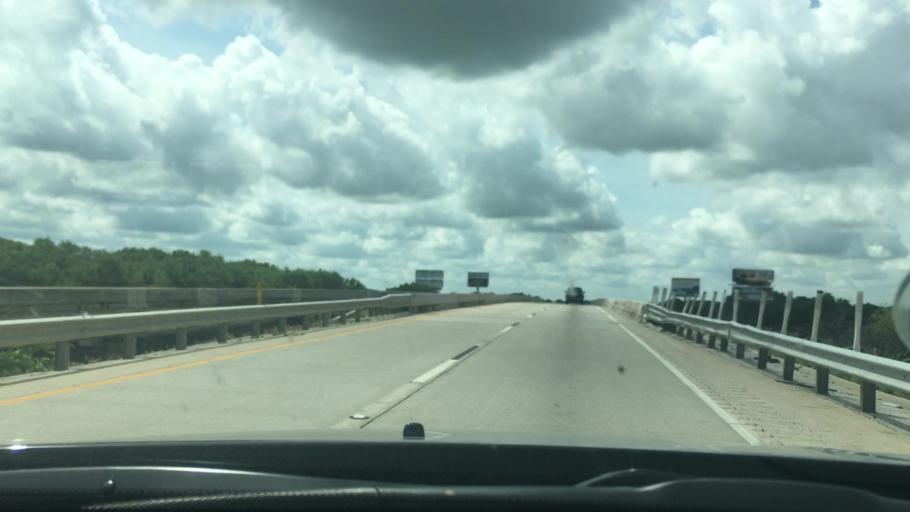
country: US
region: Oklahoma
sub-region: Love County
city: Marietta
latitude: 33.8364
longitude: -97.1323
